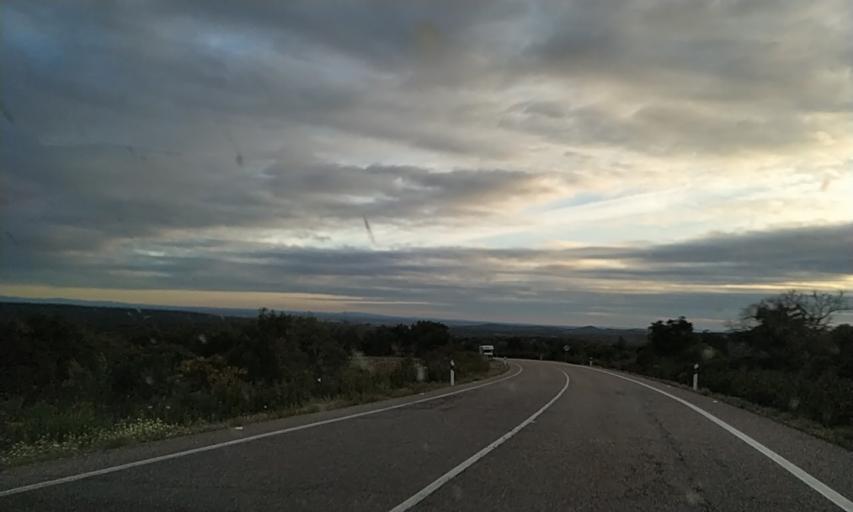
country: ES
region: Extremadura
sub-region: Provincia de Badajoz
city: Puebla de Obando
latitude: 39.1635
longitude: -6.6392
